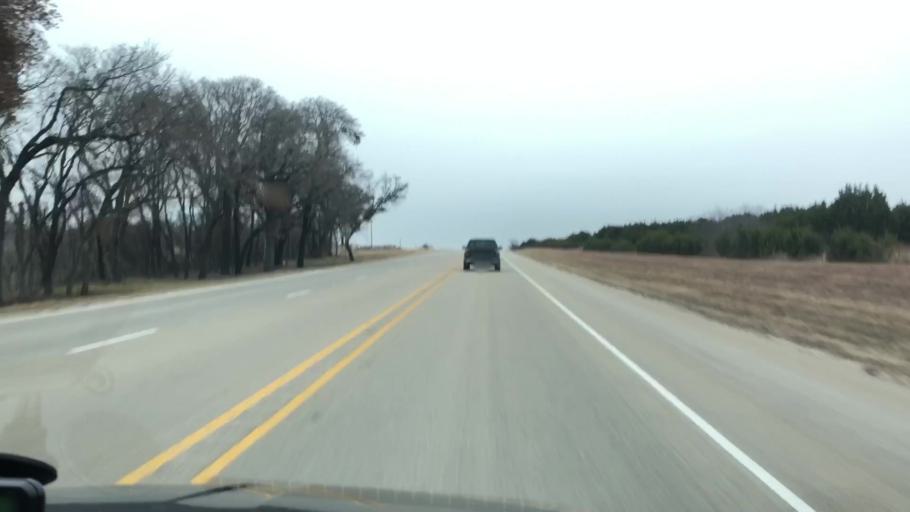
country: US
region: Texas
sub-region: Hamilton County
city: Hamilton
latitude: 31.6207
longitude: -98.1570
